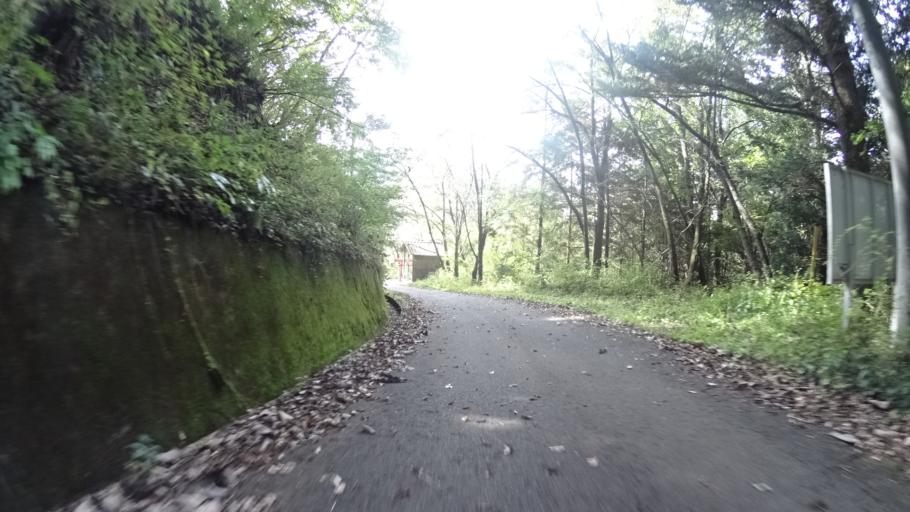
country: JP
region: Yamanashi
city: Otsuki
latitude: 35.5731
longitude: 138.9904
